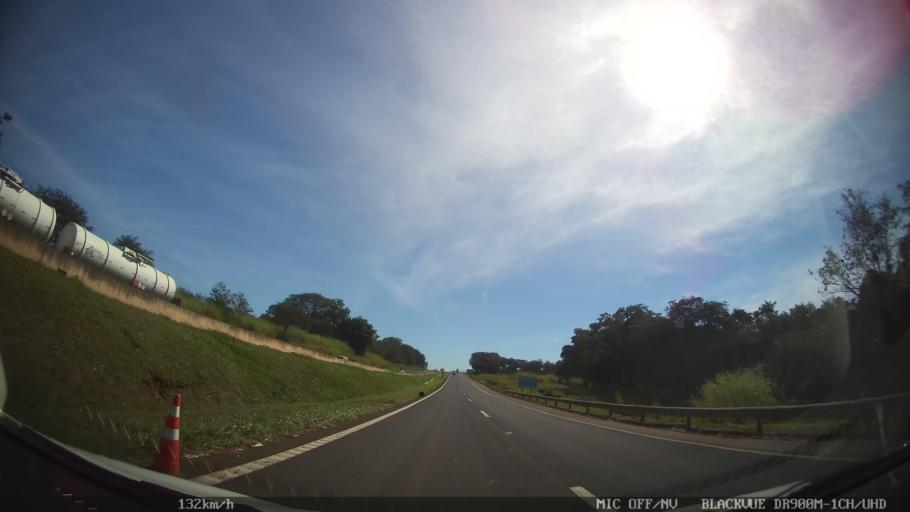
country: BR
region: Sao Paulo
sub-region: Porto Ferreira
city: Porto Ferreira
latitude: -21.9163
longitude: -47.4736
